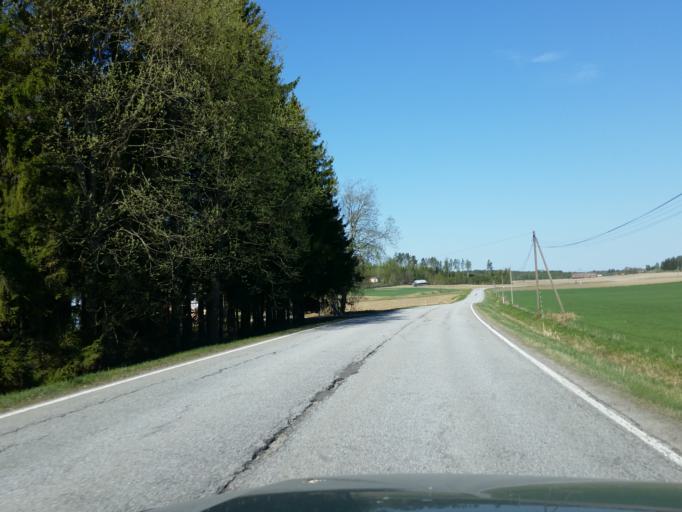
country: FI
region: Uusimaa
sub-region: Helsinki
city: Lohja
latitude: 60.1764
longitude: 24.0580
